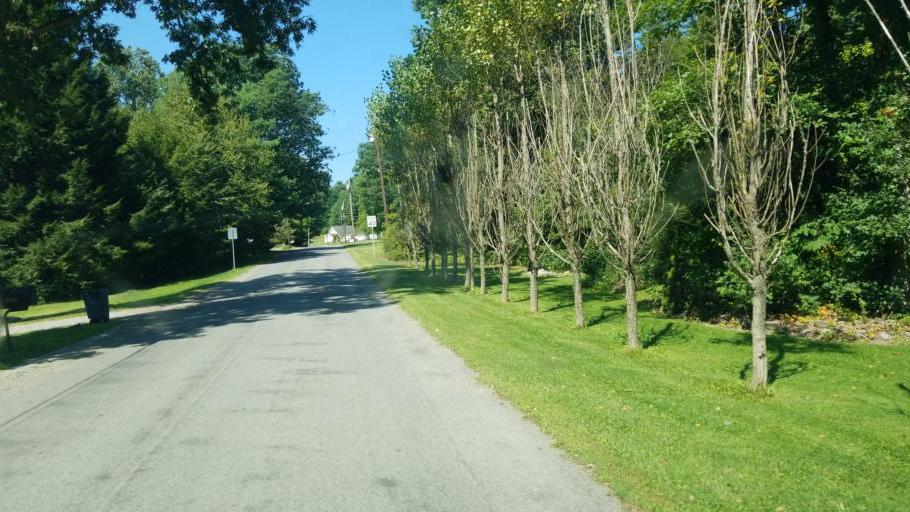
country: US
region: Pennsylvania
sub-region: Clarion County
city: Clarion
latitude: 41.1727
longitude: -79.4254
